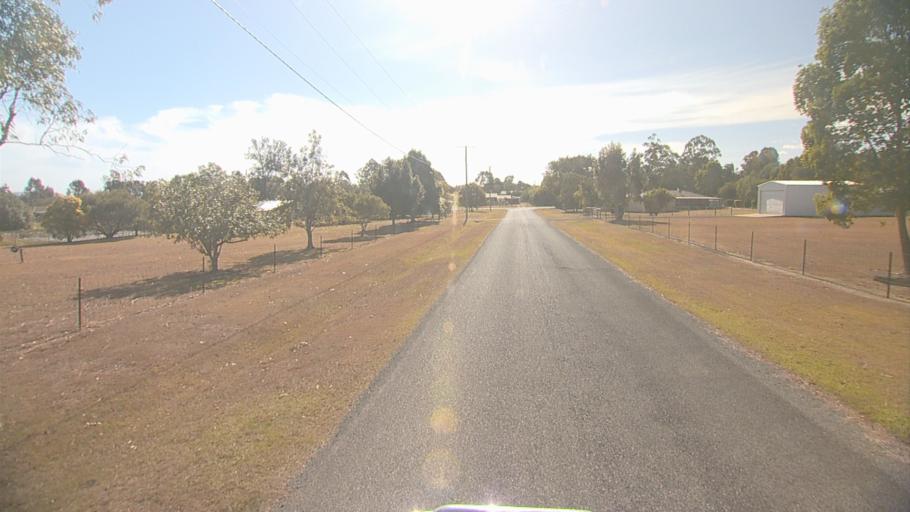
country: AU
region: Queensland
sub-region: Logan
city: Cedar Vale
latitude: -27.8693
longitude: 152.9686
